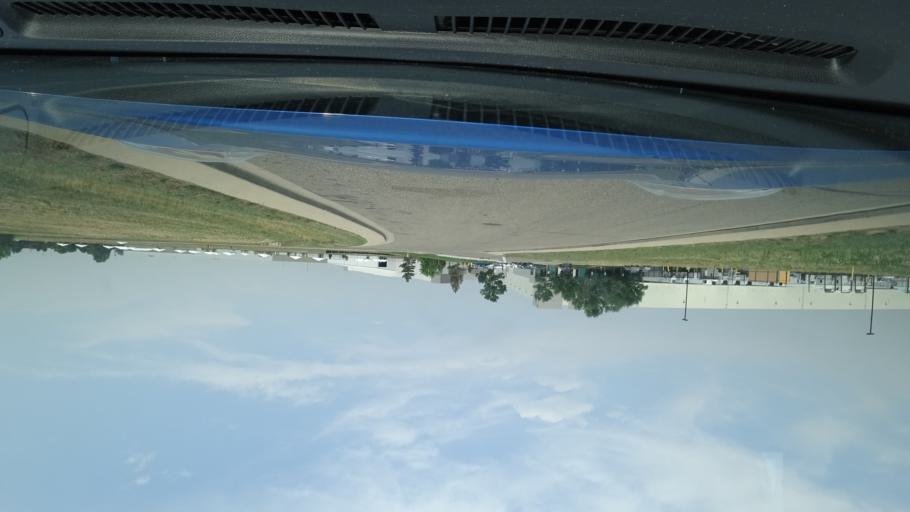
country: US
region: Colorado
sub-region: Adams County
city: Aurora
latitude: 39.7621
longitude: -104.7474
